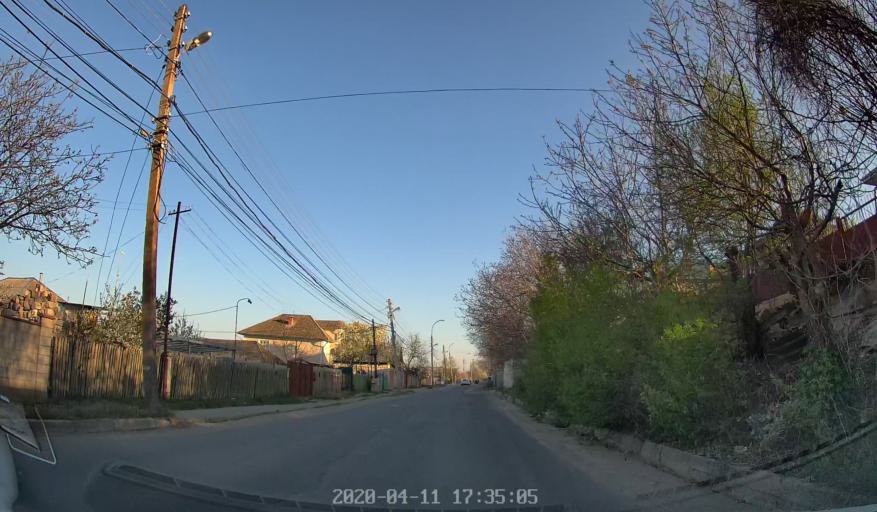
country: MD
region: Laloveni
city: Ialoveni
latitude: 46.9921
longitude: 28.8031
